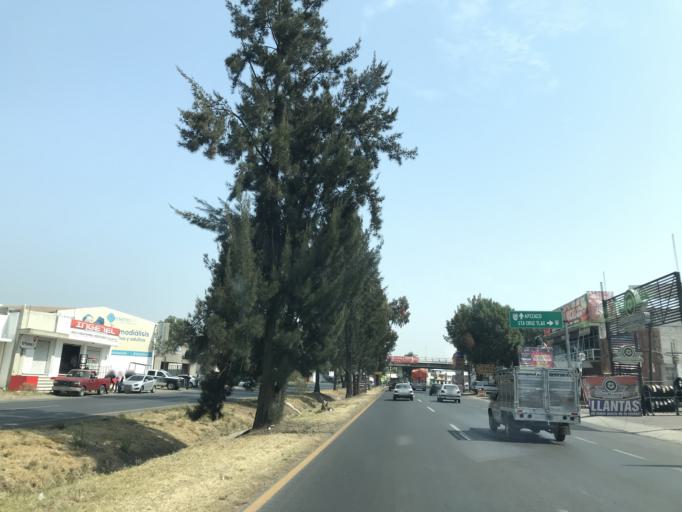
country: MX
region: Tlaxcala
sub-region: Apetatitlan de Antonio Carvajal
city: Tlatempan
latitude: 19.3275
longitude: -98.2002
